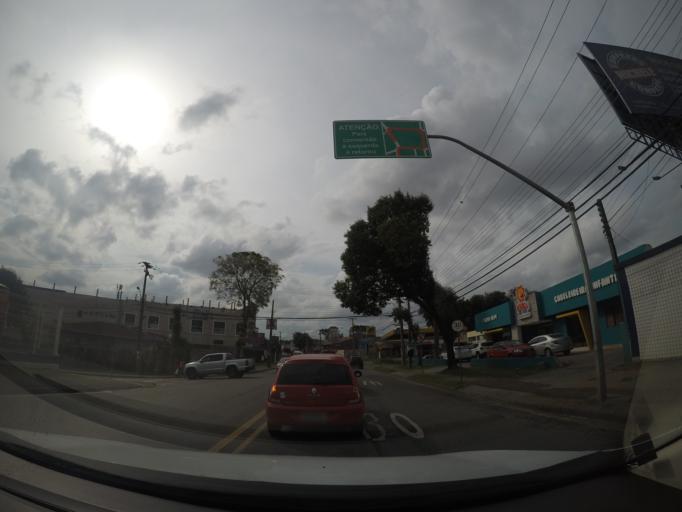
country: BR
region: Parana
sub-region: Sao Jose Dos Pinhais
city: Sao Jose dos Pinhais
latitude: -25.5195
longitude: -49.2552
